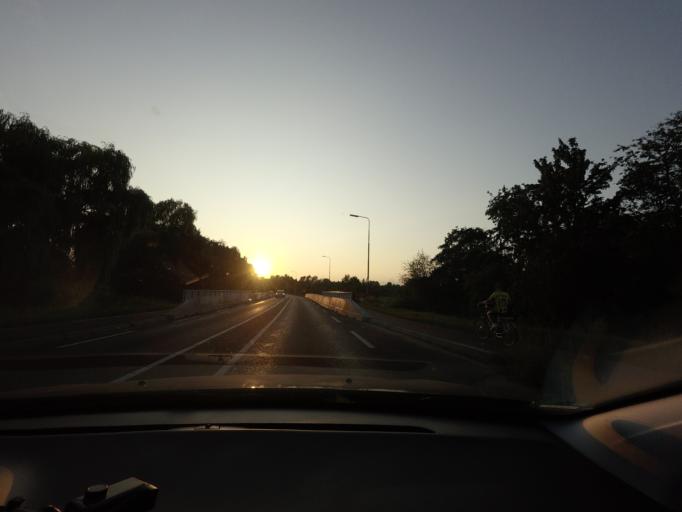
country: NL
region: Gelderland
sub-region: Gemeente Tiel
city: Tiel
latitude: 51.8853
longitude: 5.4018
